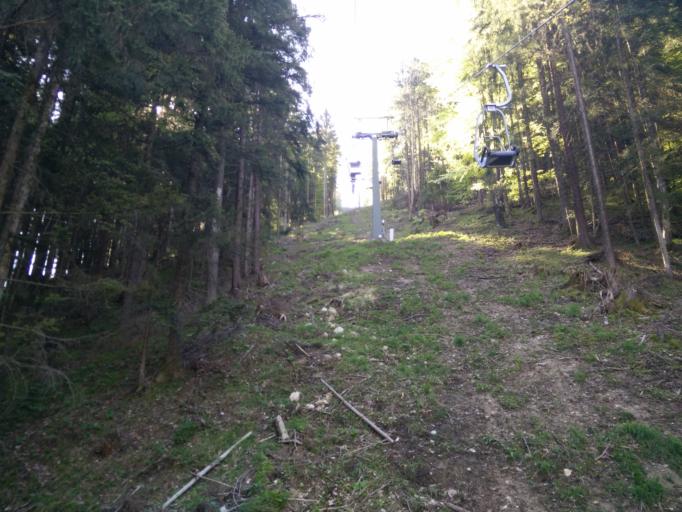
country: AT
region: Tyrol
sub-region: Politischer Bezirk Kufstein
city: Kufstein
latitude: 47.5887
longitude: 12.1891
